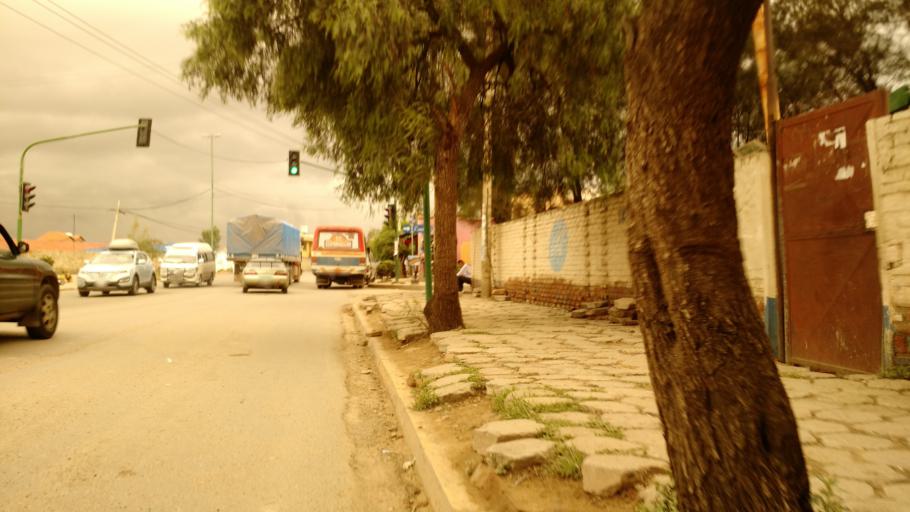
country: BO
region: Cochabamba
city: Cochabamba
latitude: -17.4224
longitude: -66.1665
